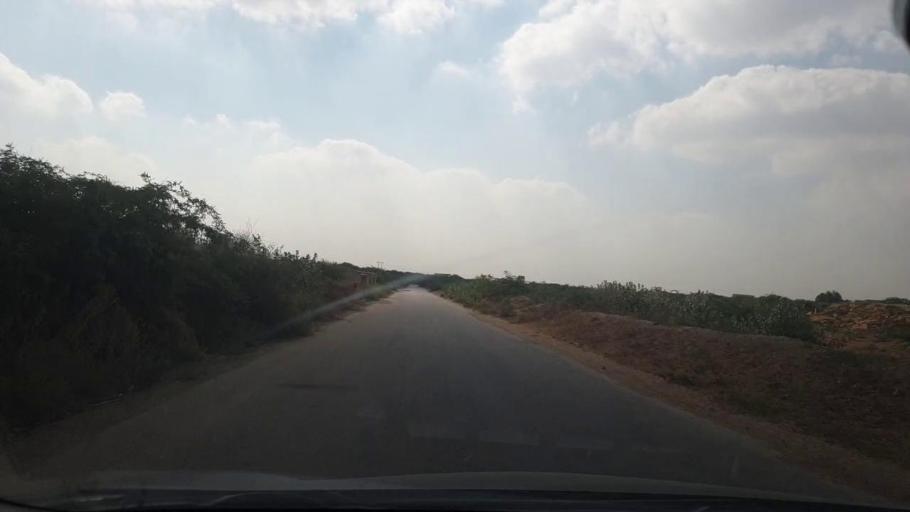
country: PK
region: Sindh
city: Malir Cantonment
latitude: 25.0179
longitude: 67.3537
